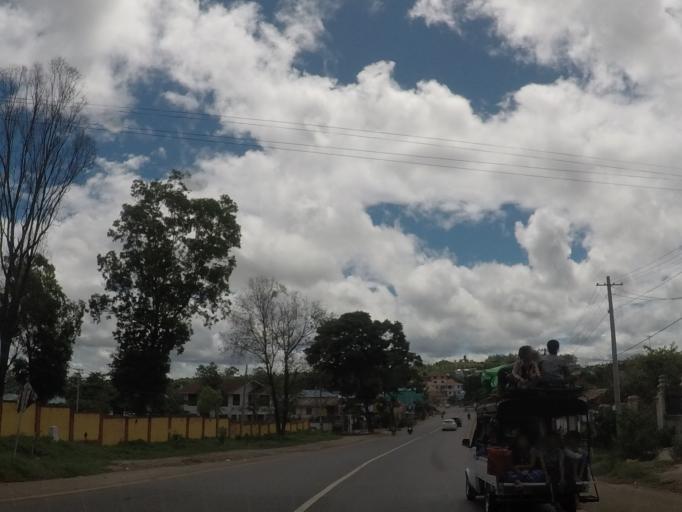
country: MM
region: Mandalay
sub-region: Pyin Oo Lwin District
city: Pyin Oo Lwin
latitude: 22.0415
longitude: 96.4991
